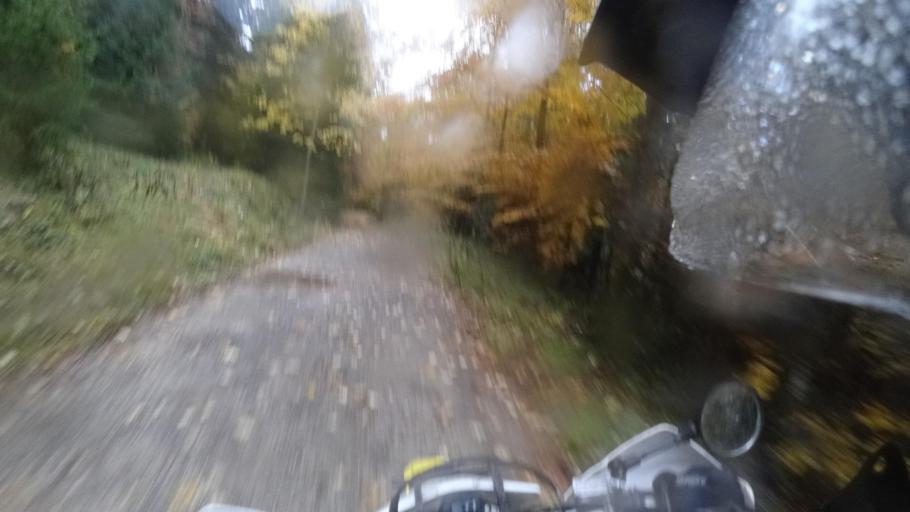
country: HR
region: Primorsko-Goranska
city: Vrbovsko
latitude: 45.2999
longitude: 14.9707
